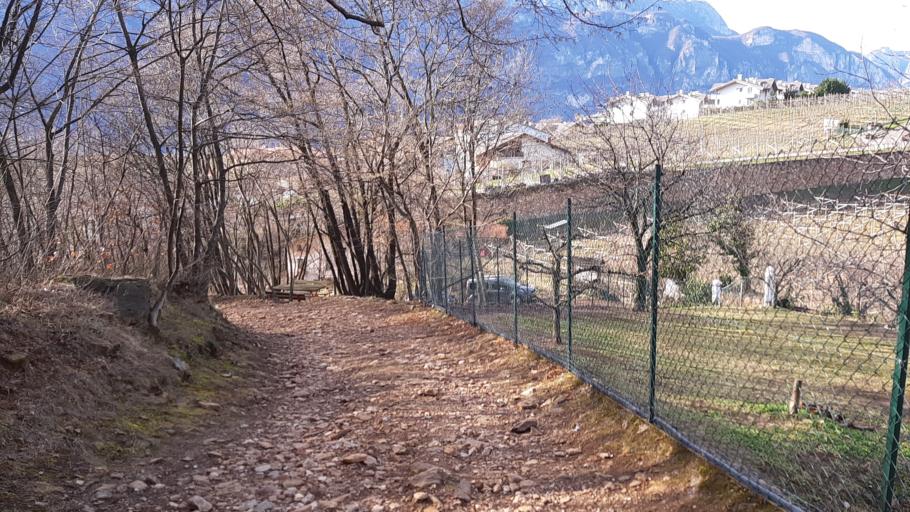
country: IT
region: Trentino-Alto Adige
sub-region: Provincia di Trento
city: Lavis
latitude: 46.1478
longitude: 11.1130
